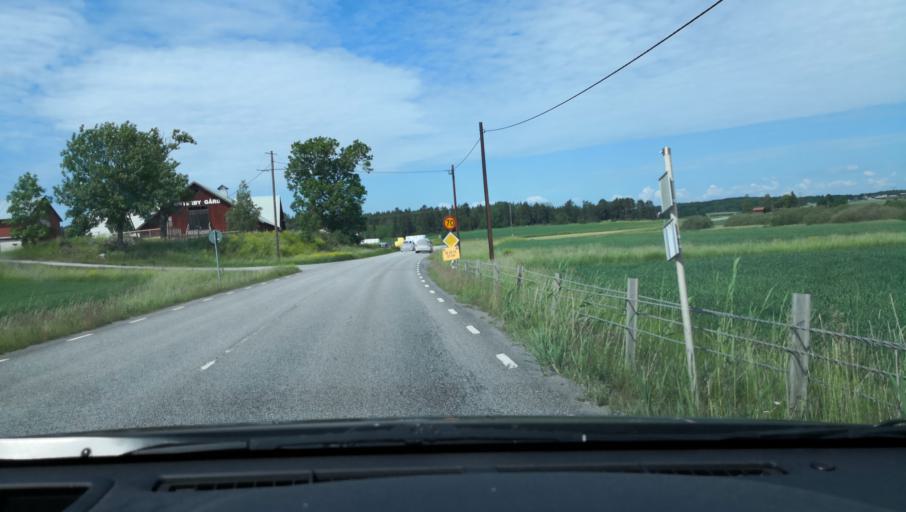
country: SE
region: Stockholm
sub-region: Sigtuna Kommun
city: Sigtuna
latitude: 59.6594
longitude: 17.6904
